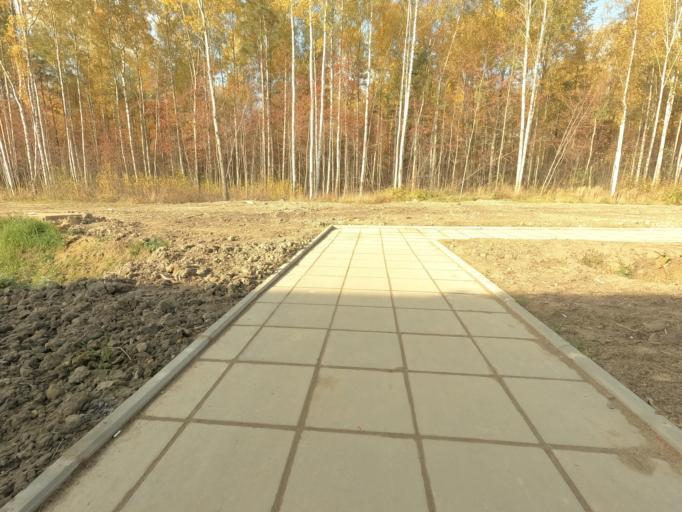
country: RU
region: Leningrad
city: Mga
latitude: 59.7599
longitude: 31.1139
